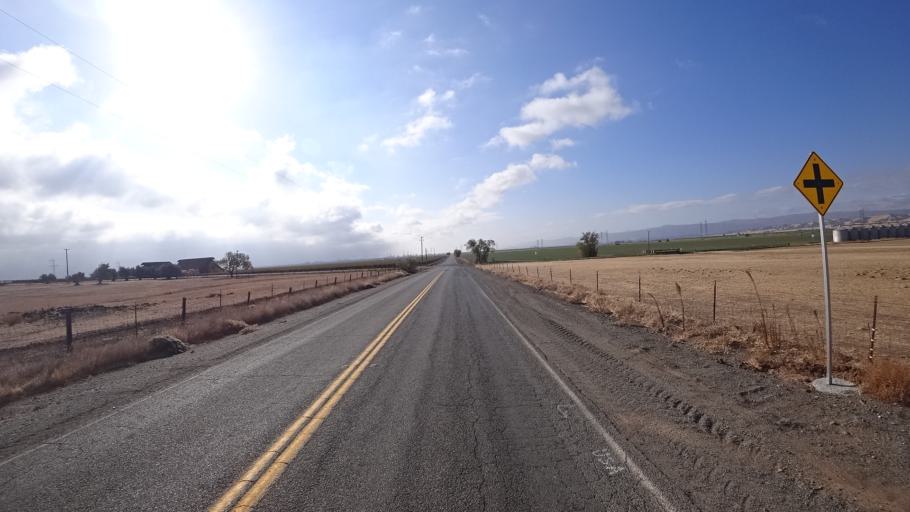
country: US
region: California
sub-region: Yolo County
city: Esparto
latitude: 38.7820
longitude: -122.0073
